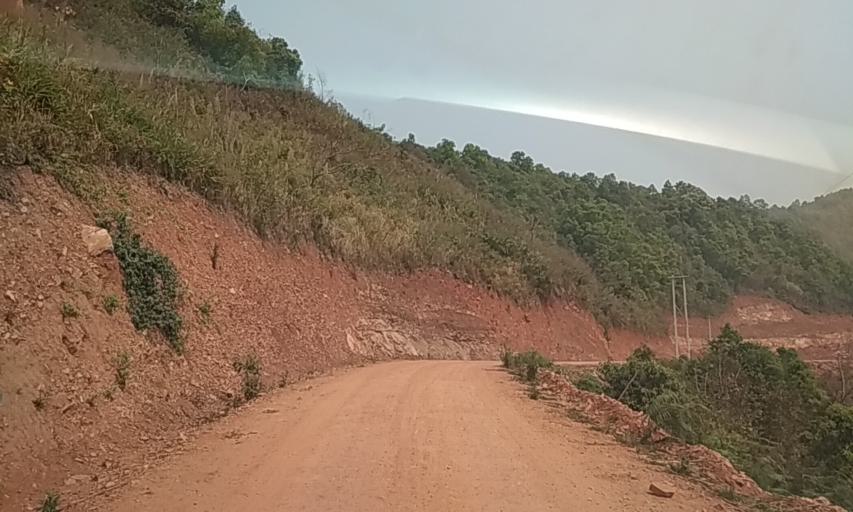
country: VN
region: Huyen Dien Bien
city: Dien Bien Phu
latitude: 21.4968
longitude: 102.7866
